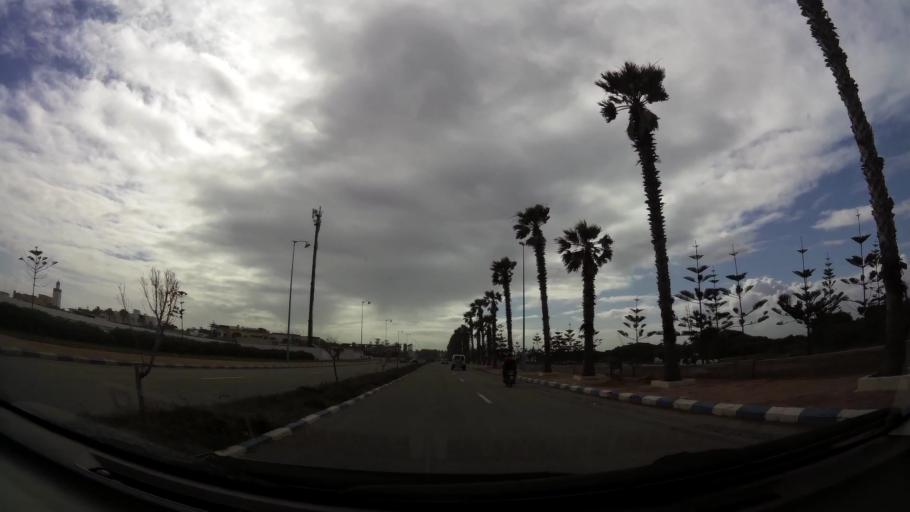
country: MA
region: Doukkala-Abda
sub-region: El-Jadida
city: El Jadida
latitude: 33.2440
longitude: -8.4677
